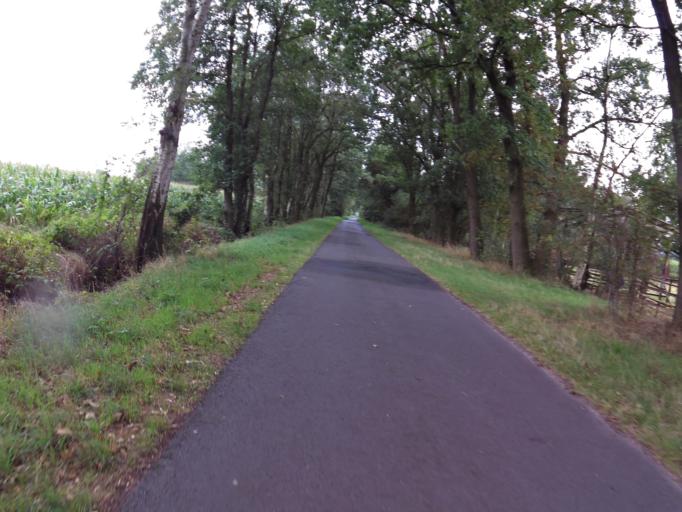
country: DE
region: Lower Saxony
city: Hamersen
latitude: 53.2642
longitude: 9.4755
